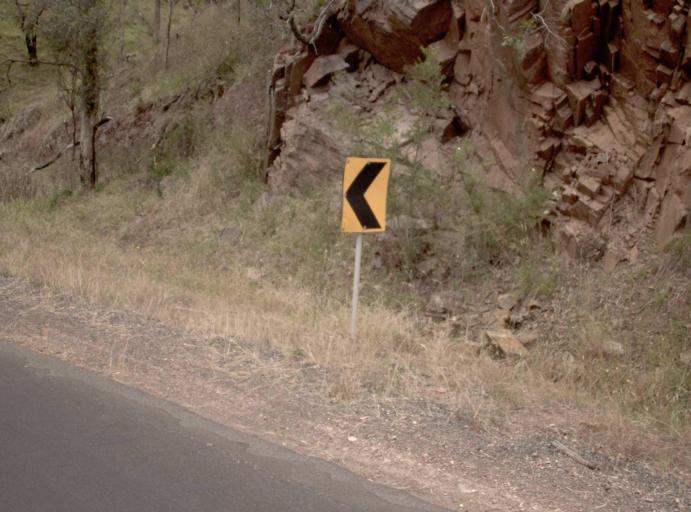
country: AU
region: Victoria
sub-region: Wellington
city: Heyfield
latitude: -37.7025
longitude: 146.6681
